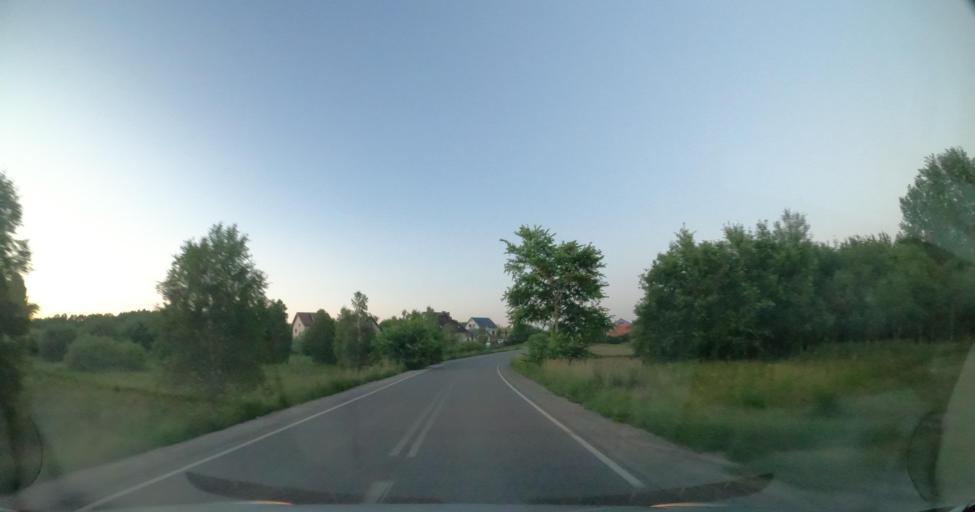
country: PL
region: Pomeranian Voivodeship
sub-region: Powiat wejherowski
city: Szemud
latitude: 54.4759
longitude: 18.1789
